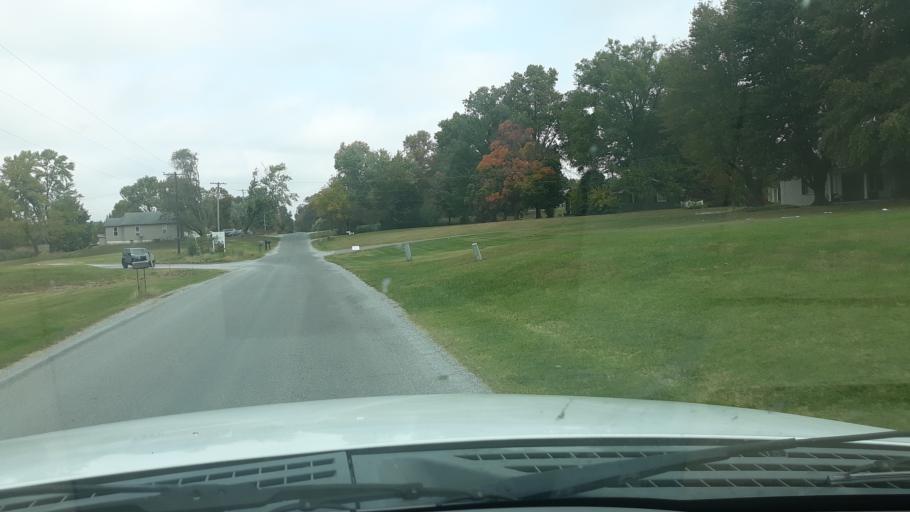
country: US
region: Illinois
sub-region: Saline County
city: Eldorado
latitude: 37.8254
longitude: -88.4848
